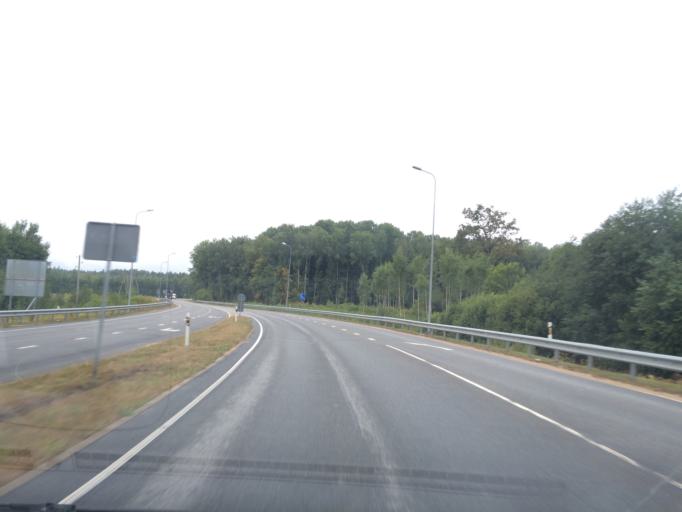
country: LV
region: Ogre
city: Ogre
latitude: 56.8587
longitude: 24.6422
